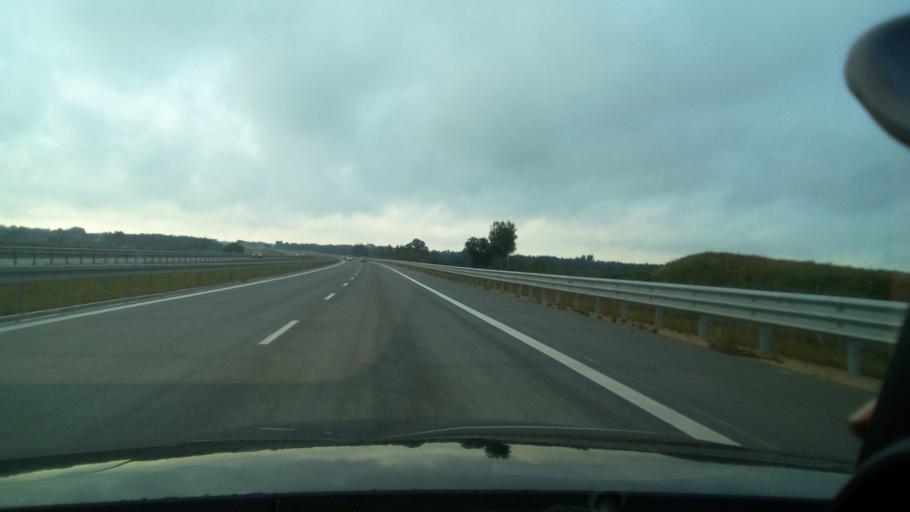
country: PL
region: Silesian Voivodeship
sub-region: Powiat czestochowski
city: Konopiska
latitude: 50.7564
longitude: 19.0260
